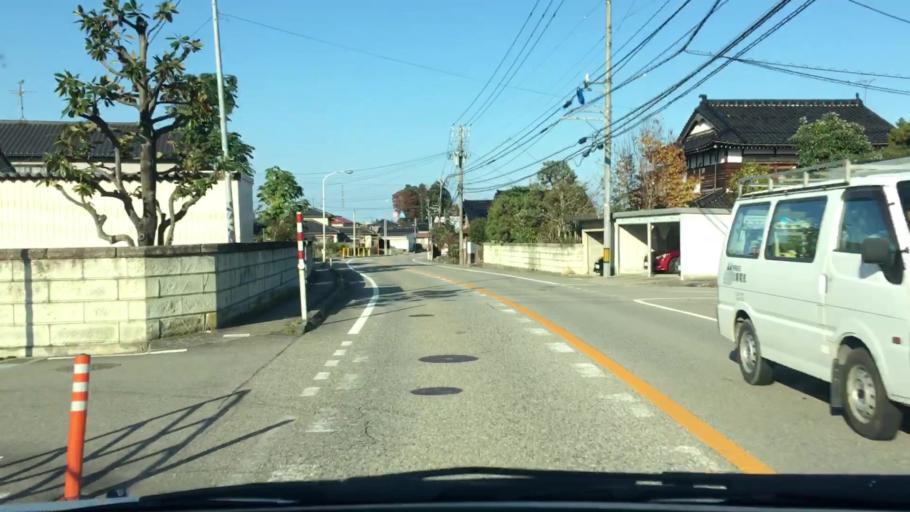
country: JP
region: Toyama
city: Kamiichi
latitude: 36.7051
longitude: 137.3115
